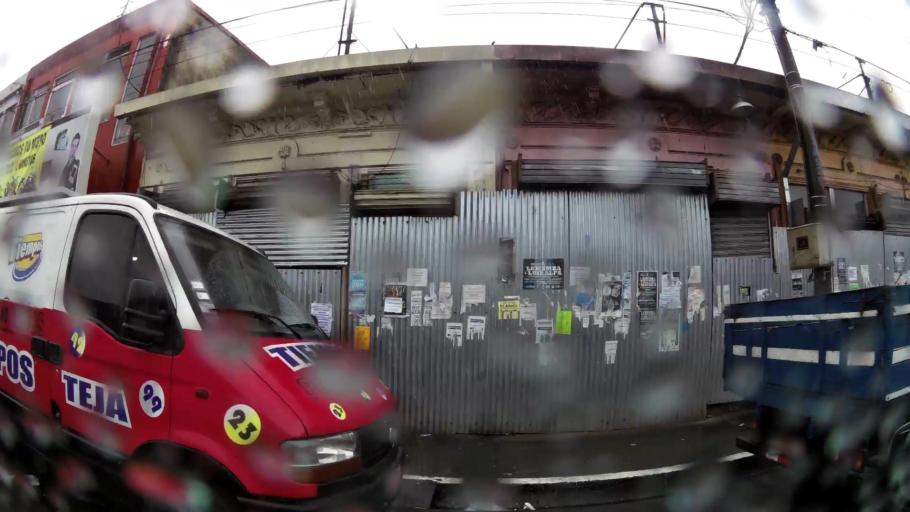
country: CR
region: Cartago
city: Cartago
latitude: 9.8656
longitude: -83.9214
